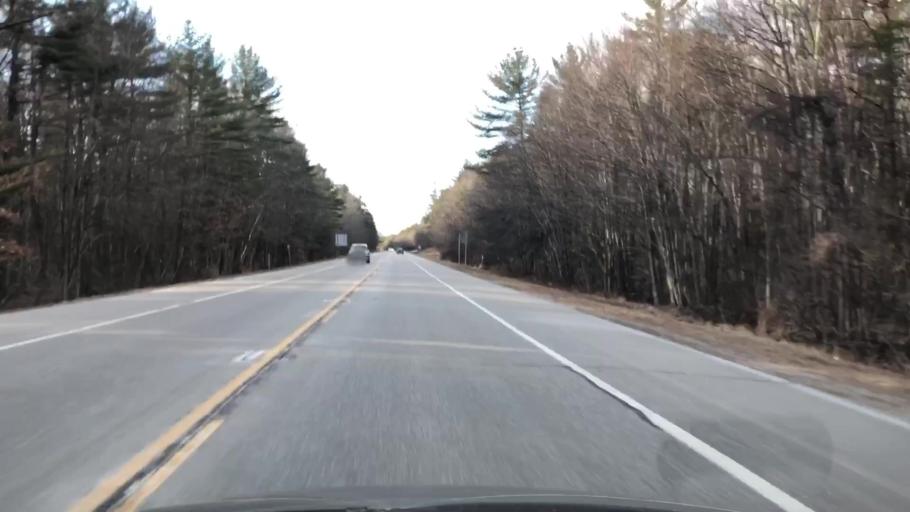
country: US
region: New Hampshire
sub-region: Hillsborough County
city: Milford
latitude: 42.8266
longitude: -71.6665
